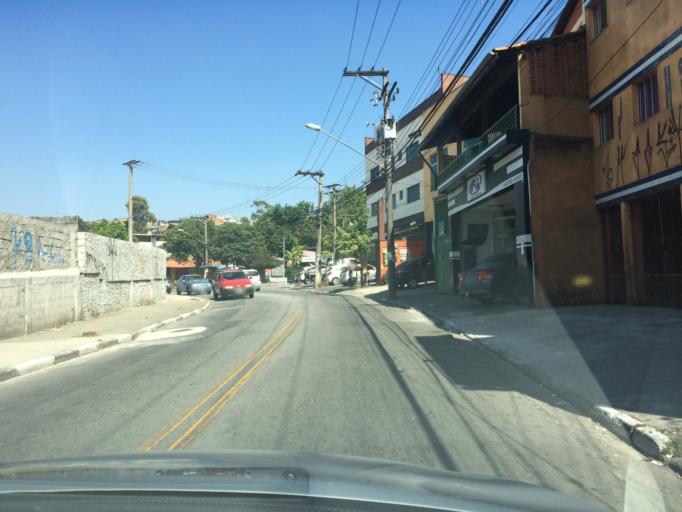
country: BR
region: Sao Paulo
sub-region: Guarulhos
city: Guarulhos
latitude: -23.4316
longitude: -46.5388
